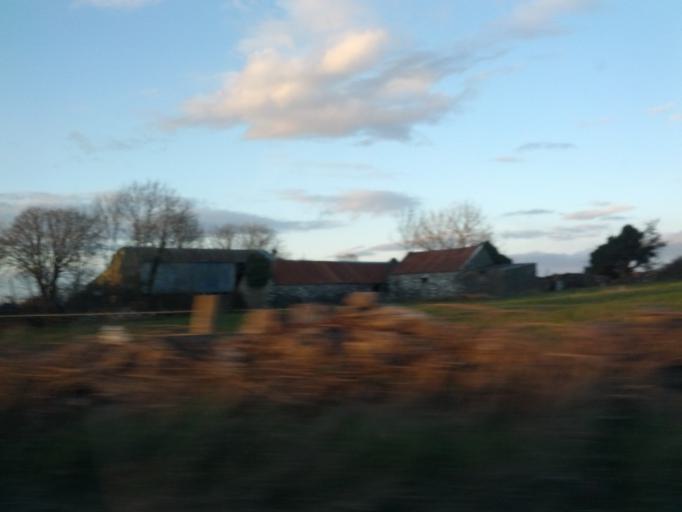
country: IE
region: Connaught
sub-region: County Galway
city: Athenry
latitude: 53.2716
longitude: -8.6923
